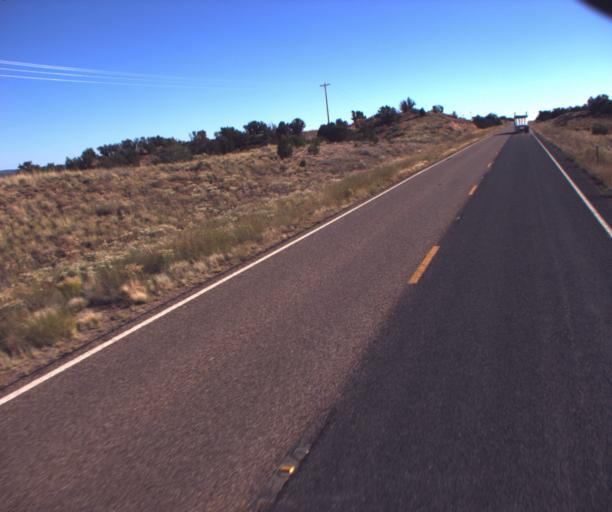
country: US
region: Arizona
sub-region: Apache County
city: Ganado
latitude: 35.4528
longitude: -109.5220
